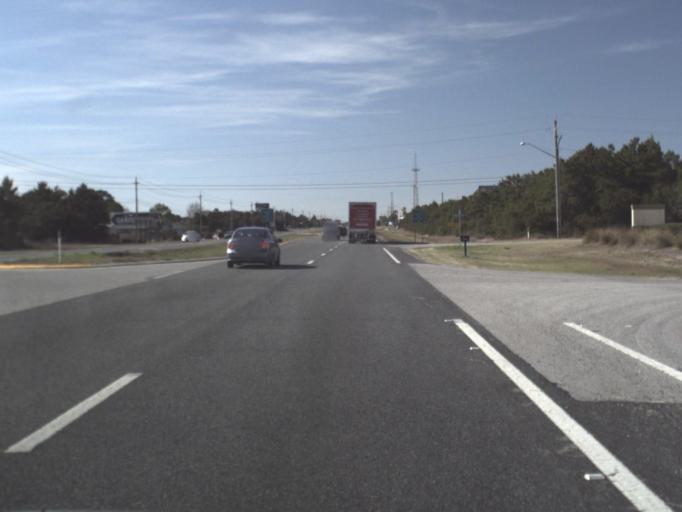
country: US
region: Florida
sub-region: Bay County
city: Laguna Beach
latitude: 30.2437
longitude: -85.9191
